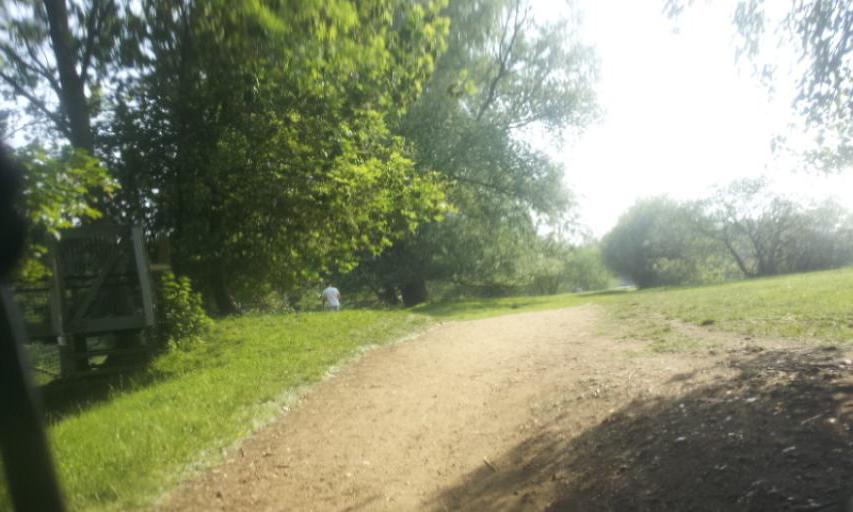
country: GB
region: England
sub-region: Kent
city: Chartham
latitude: 51.2614
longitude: 1.0354
